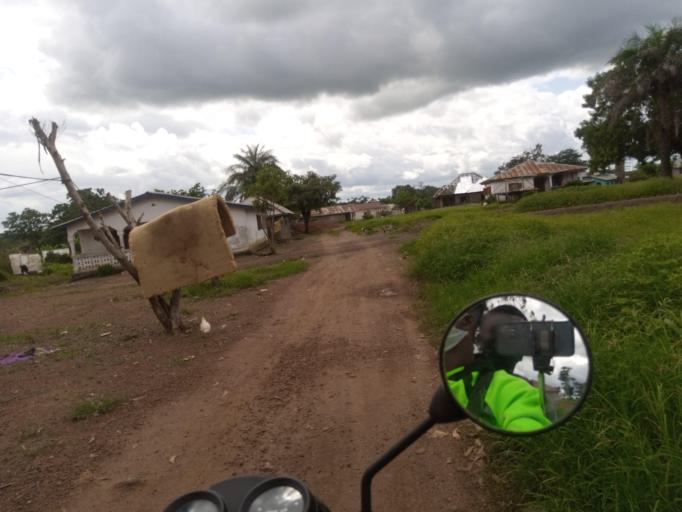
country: SL
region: Northern Province
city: Port Loko
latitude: 8.7745
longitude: -12.7735
